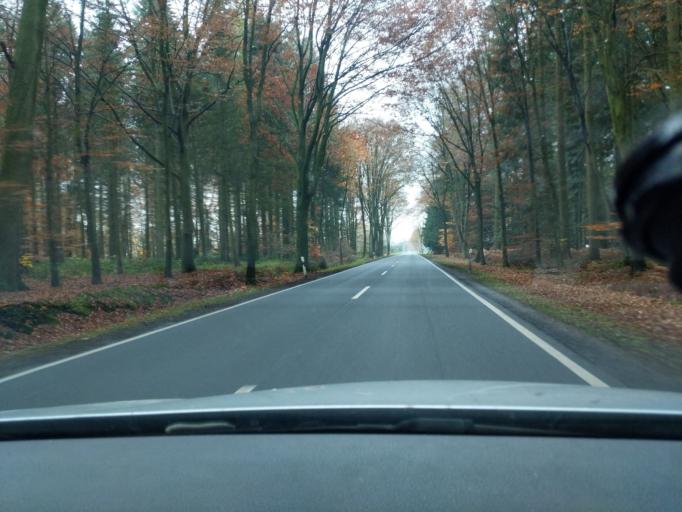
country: DE
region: Lower Saxony
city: Heeslingen
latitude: 53.3294
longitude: 9.3581
